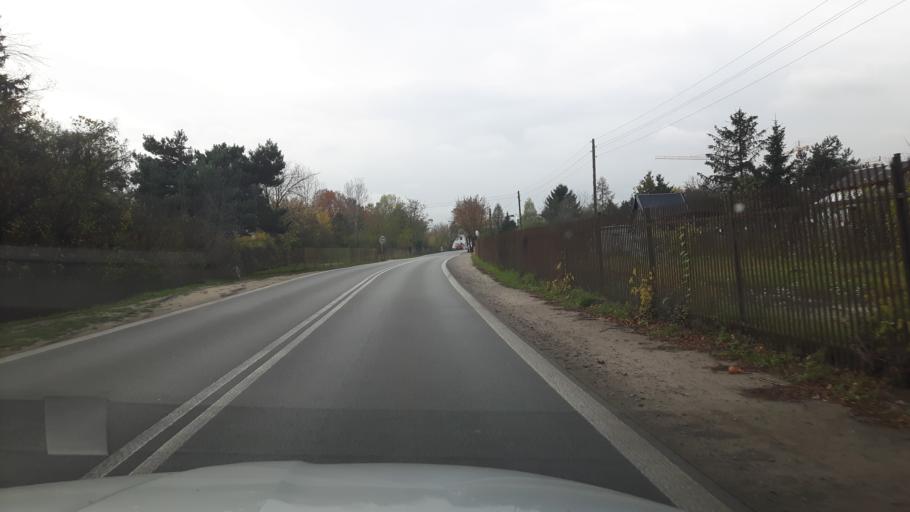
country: PL
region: Masovian Voivodeship
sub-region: Powiat wolominski
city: Zabki
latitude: 52.2784
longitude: 21.0935
